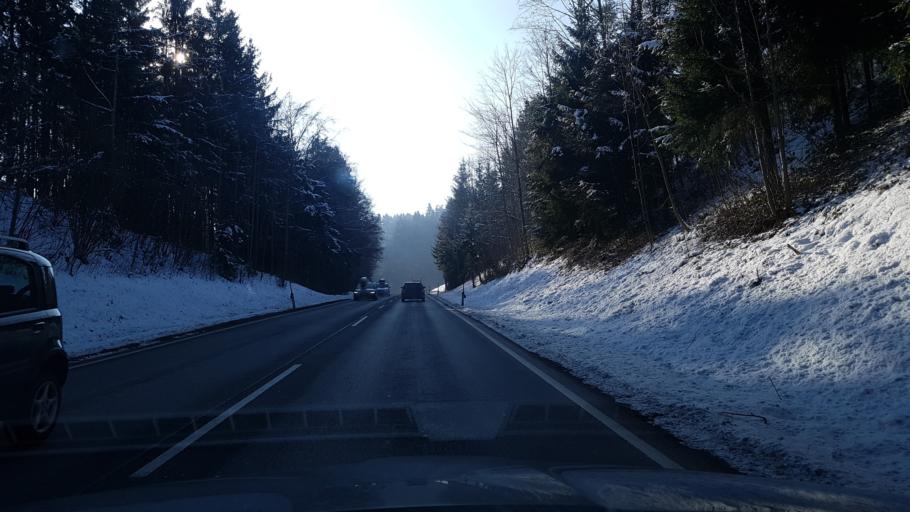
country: AT
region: Salzburg
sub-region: Politischer Bezirk Salzburg-Umgebung
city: Plainfeld
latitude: 47.8314
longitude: 13.1966
